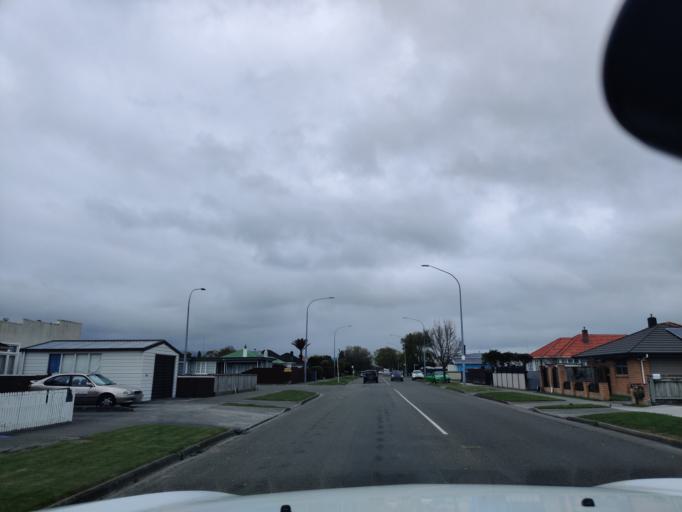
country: NZ
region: Manawatu-Wanganui
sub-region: Palmerston North City
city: Palmerston North
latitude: -40.3332
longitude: 175.6322
